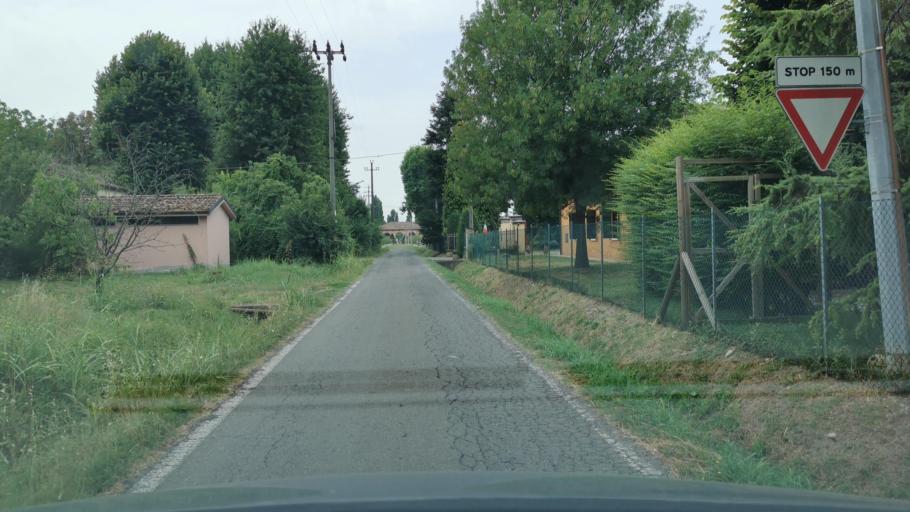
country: IT
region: Emilia-Romagna
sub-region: Provincia di Modena
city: Campogalliano
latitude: 44.6870
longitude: 10.8787
